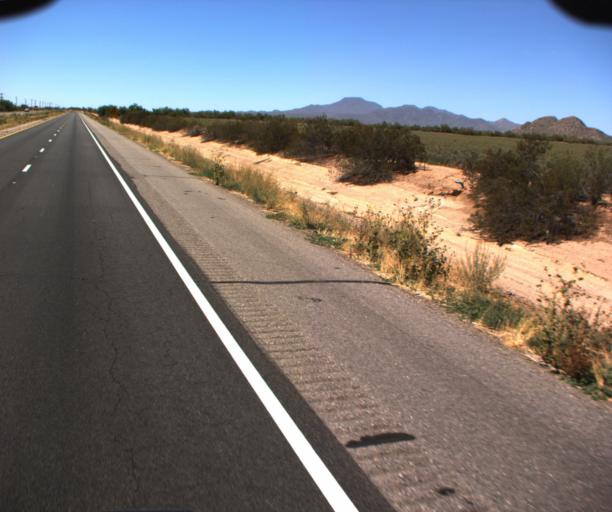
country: US
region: Arizona
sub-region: Pinal County
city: Maricopa
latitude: 32.8906
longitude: -112.0496
